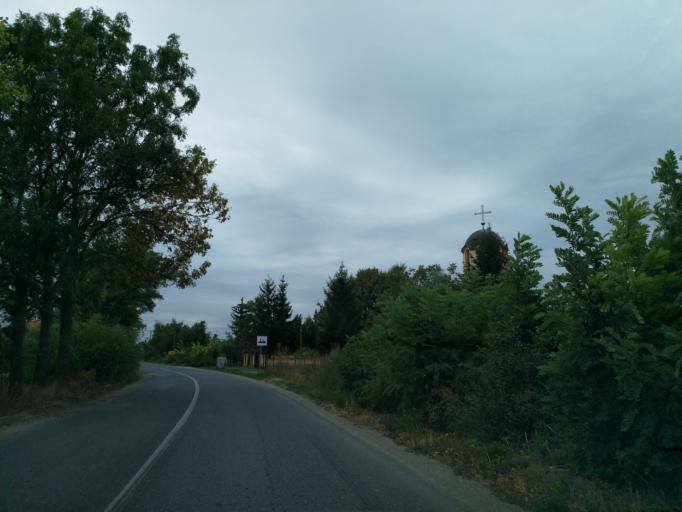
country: RS
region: Central Serbia
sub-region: Pomoravski Okrug
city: Paracin
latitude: 43.8342
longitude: 21.3660
